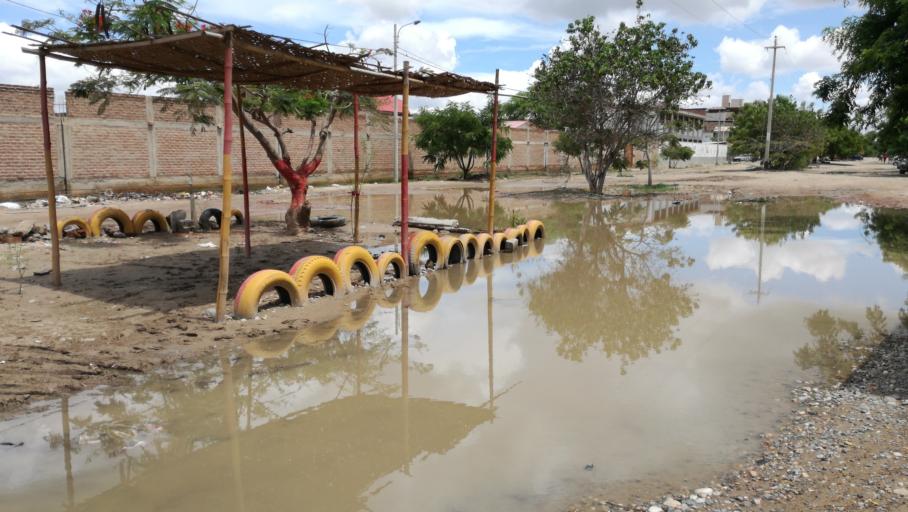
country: PE
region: Piura
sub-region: Provincia de Piura
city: Piura
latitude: -5.1802
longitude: -80.6441
